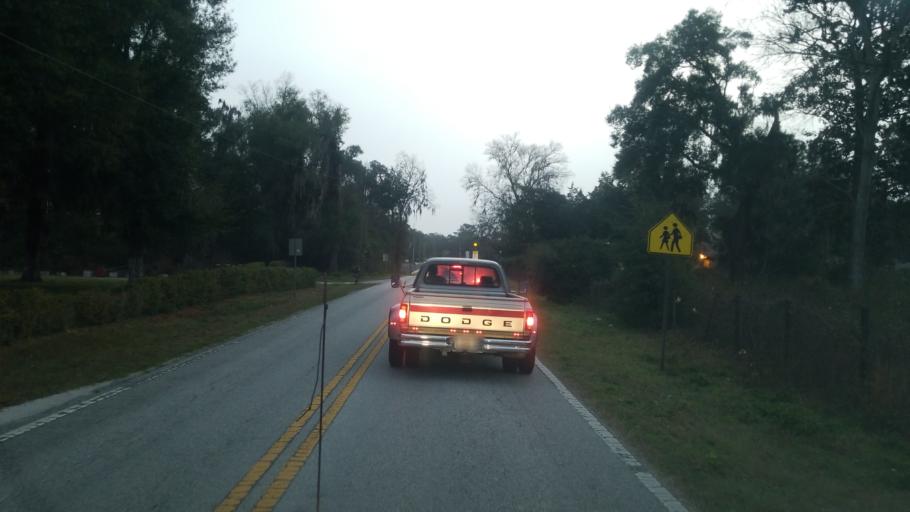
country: US
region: Florida
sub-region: Marion County
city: Ocala
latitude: 29.1482
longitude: -82.1977
